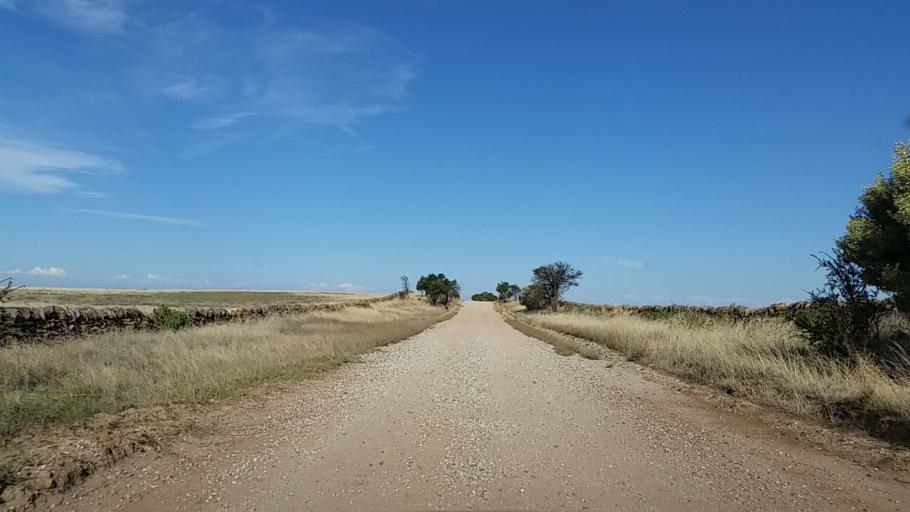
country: AU
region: South Australia
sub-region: Barossa
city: Angaston
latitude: -34.6139
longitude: 139.1962
